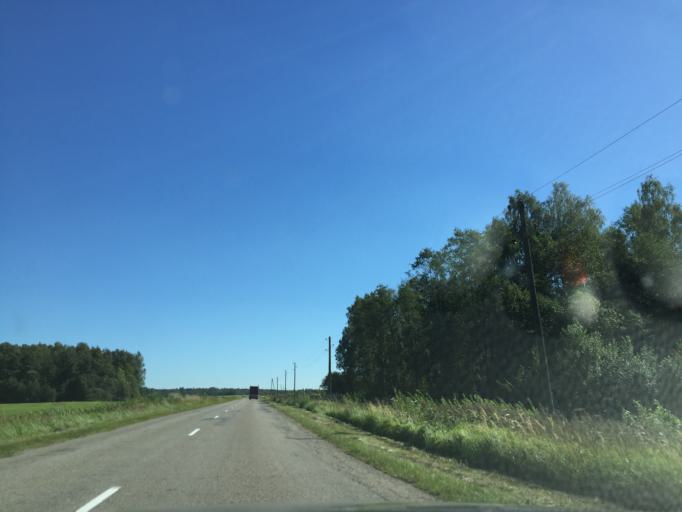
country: LV
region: Akniste
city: Akniste
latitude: 56.1096
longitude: 25.8500
